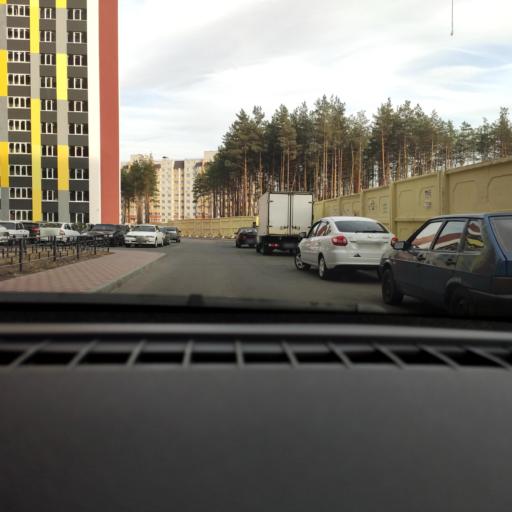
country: RU
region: Voronezj
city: Somovo
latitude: 51.7409
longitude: 39.3169
